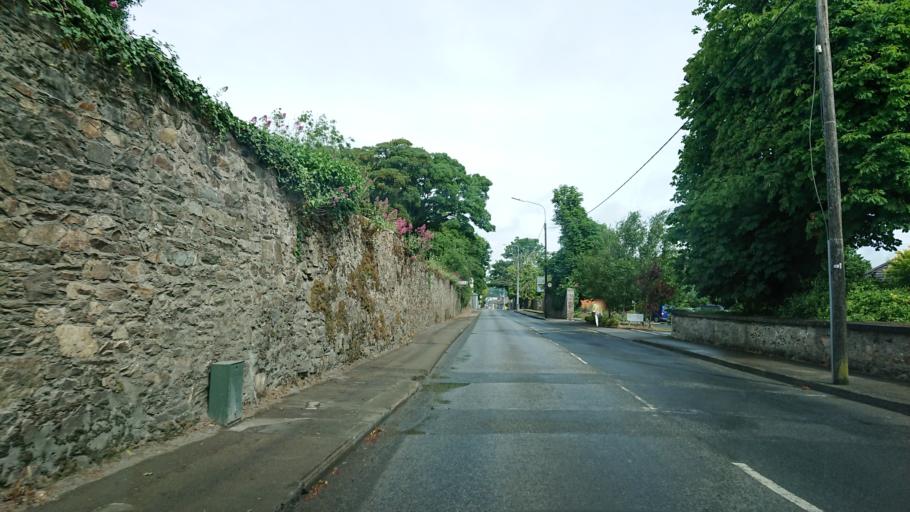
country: IE
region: Munster
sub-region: Waterford
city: Waterford
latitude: 52.2502
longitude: -7.1047
